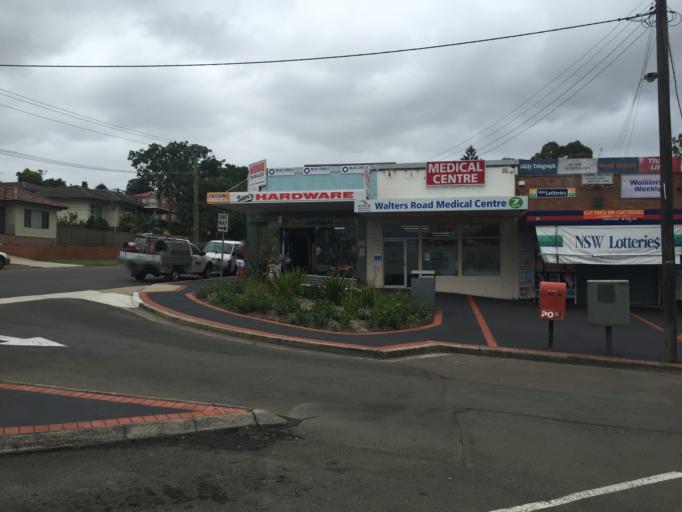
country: AU
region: New South Wales
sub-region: Blacktown
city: Blacktown
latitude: -33.7779
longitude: 150.8947
